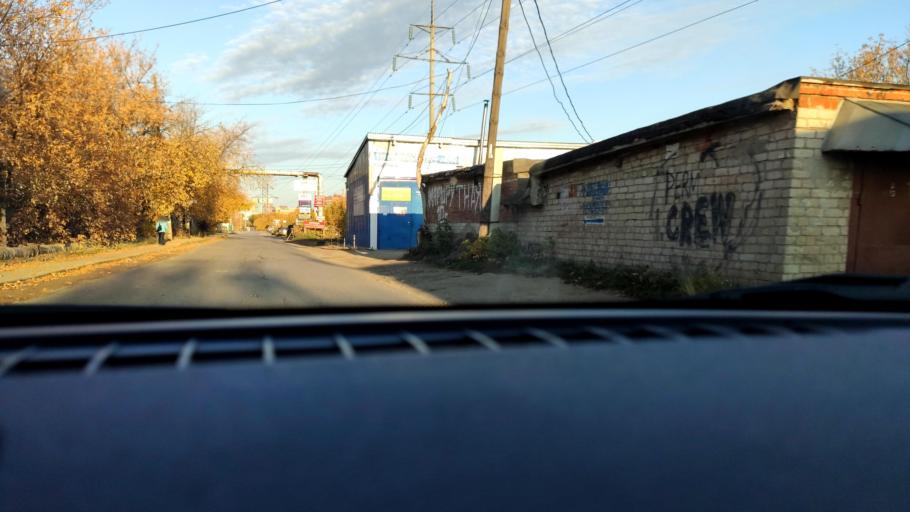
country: RU
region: Perm
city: Perm
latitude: 57.9821
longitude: 56.2418
